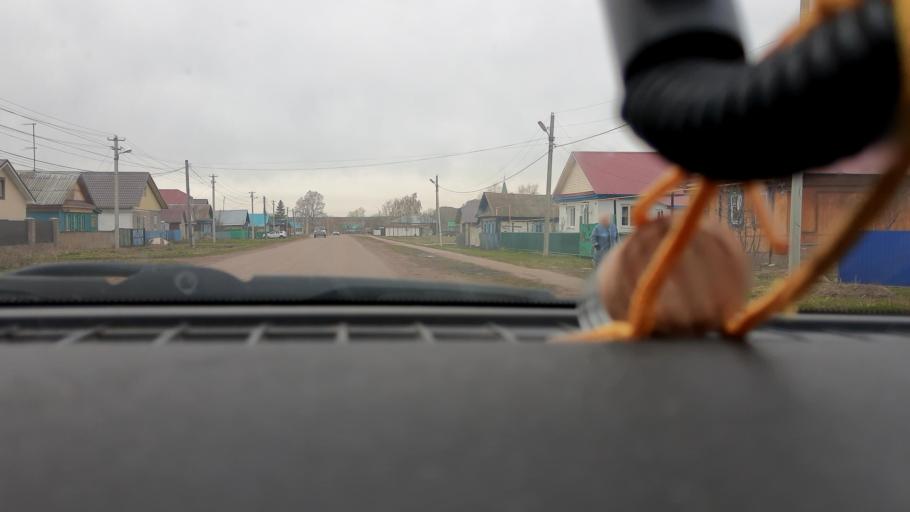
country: RU
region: Bashkortostan
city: Asanovo
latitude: 54.8135
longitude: 55.5702
